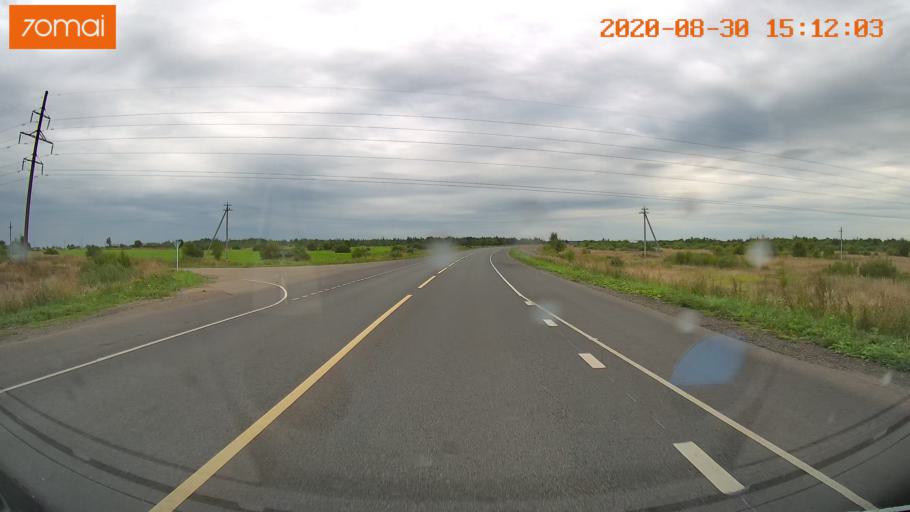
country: RU
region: Ivanovo
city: Vichuga
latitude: 57.1968
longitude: 41.8784
